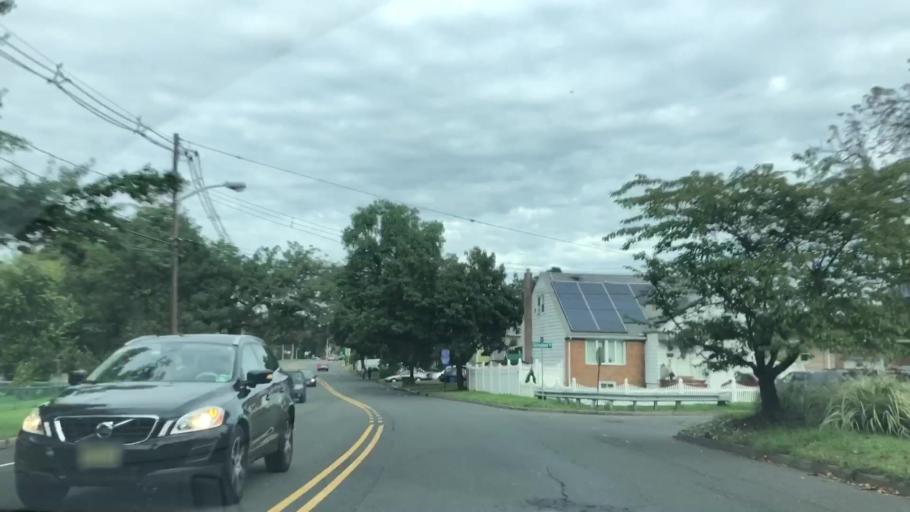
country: US
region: New Jersey
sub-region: Union County
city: Winfield
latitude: 40.6382
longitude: -74.2854
